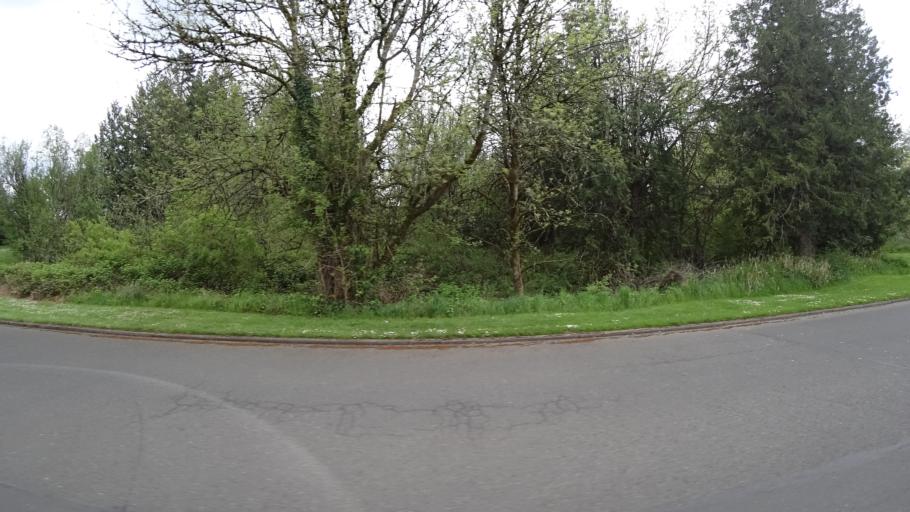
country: US
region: Oregon
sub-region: Washington County
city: Rockcreek
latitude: 45.5489
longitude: -122.8819
